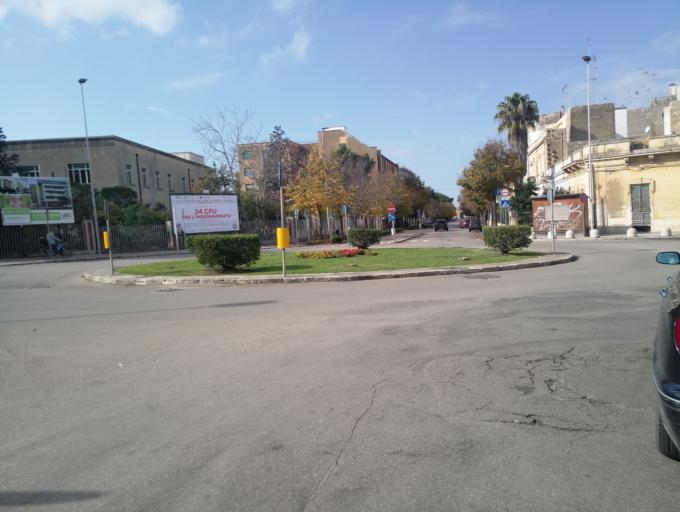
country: IT
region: Apulia
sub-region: Provincia di Lecce
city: Lecce
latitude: 40.3474
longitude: 18.1793
